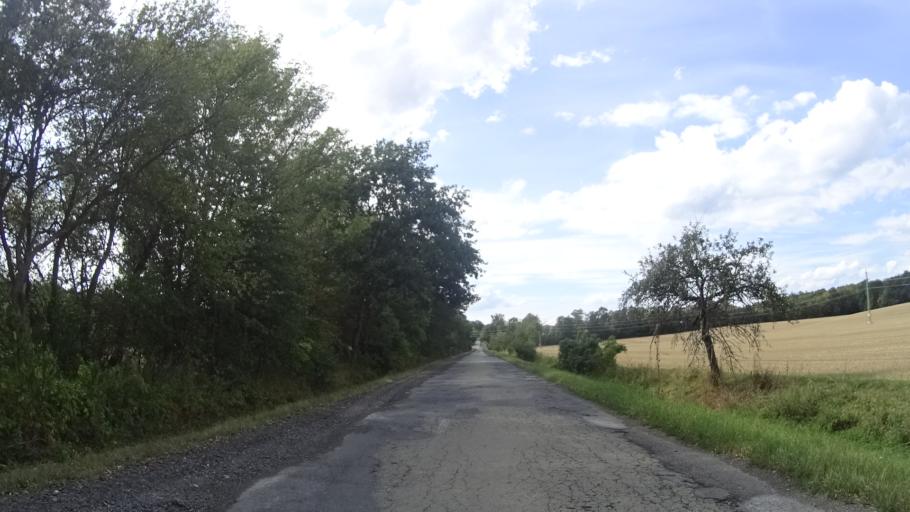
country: CZ
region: Olomoucky
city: Cervenka
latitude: 49.7190
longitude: 17.0378
